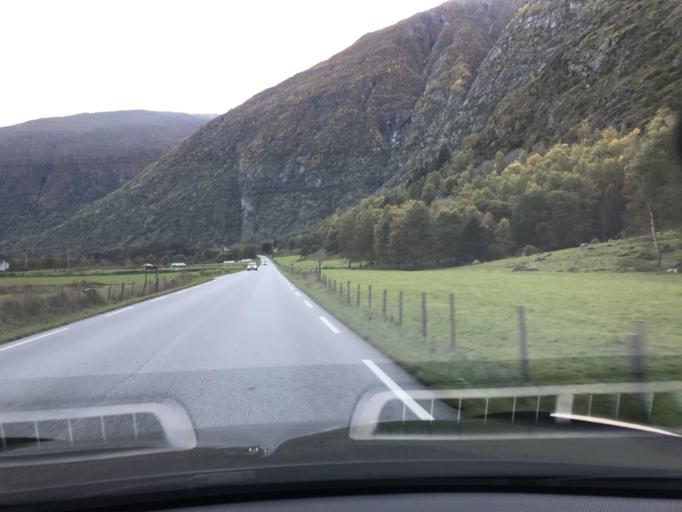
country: NO
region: Sogn og Fjordane
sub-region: Laerdal
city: Laerdalsoyri
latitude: 61.0816
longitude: 7.5069
